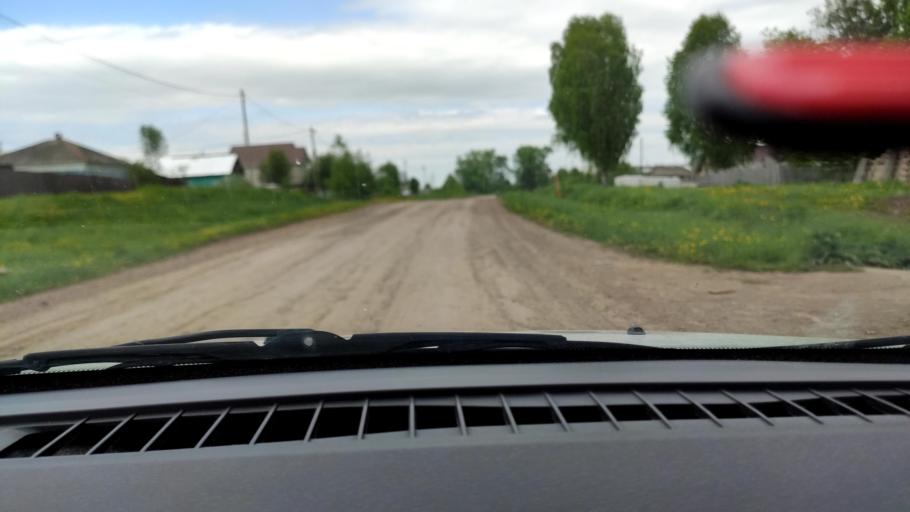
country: RU
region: Perm
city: Bershet'
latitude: 57.7291
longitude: 56.3783
